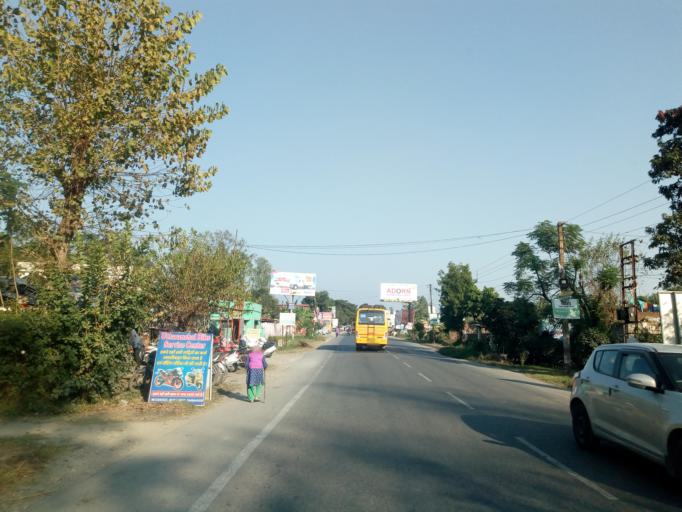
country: IN
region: Uttarakhand
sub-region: Dehradun
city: Dehradun
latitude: 30.3442
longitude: 77.9177
